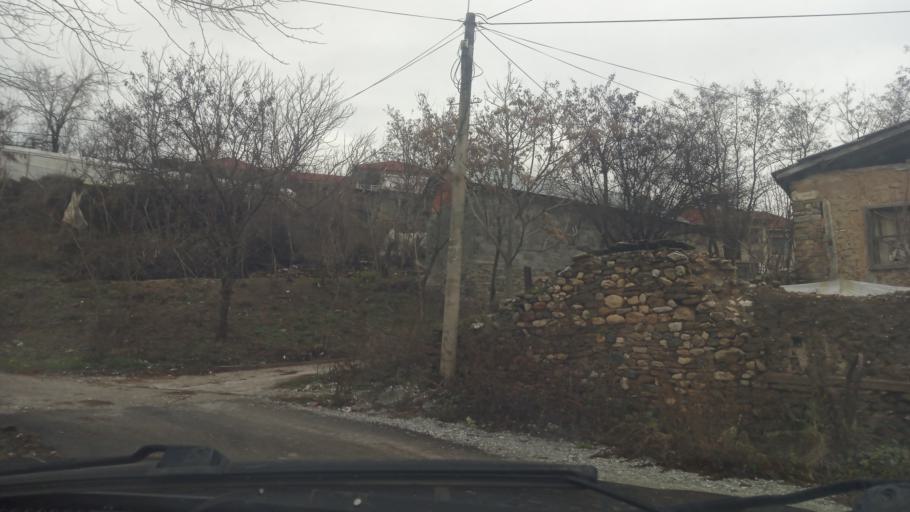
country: MK
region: Gradsko
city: Gradsko
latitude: 41.6014
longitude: 21.8977
